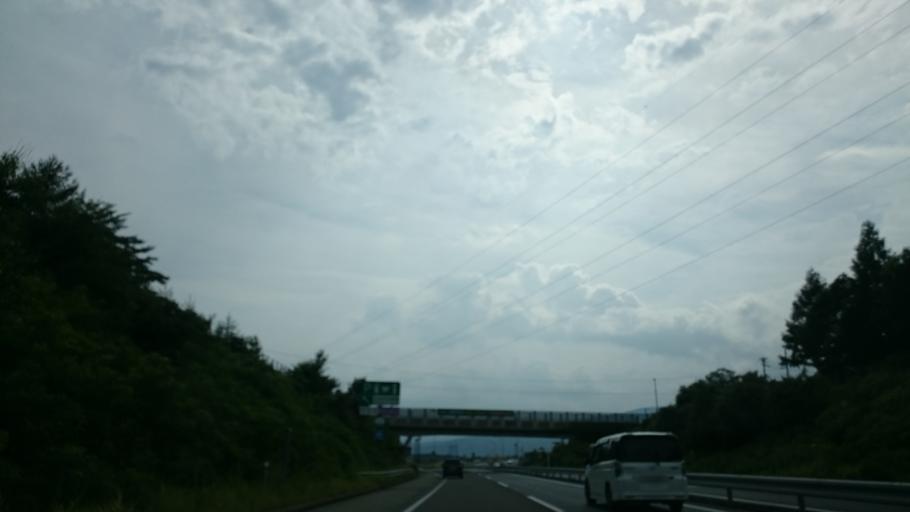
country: JP
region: Gifu
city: Gujo
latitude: 35.9900
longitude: 136.9148
